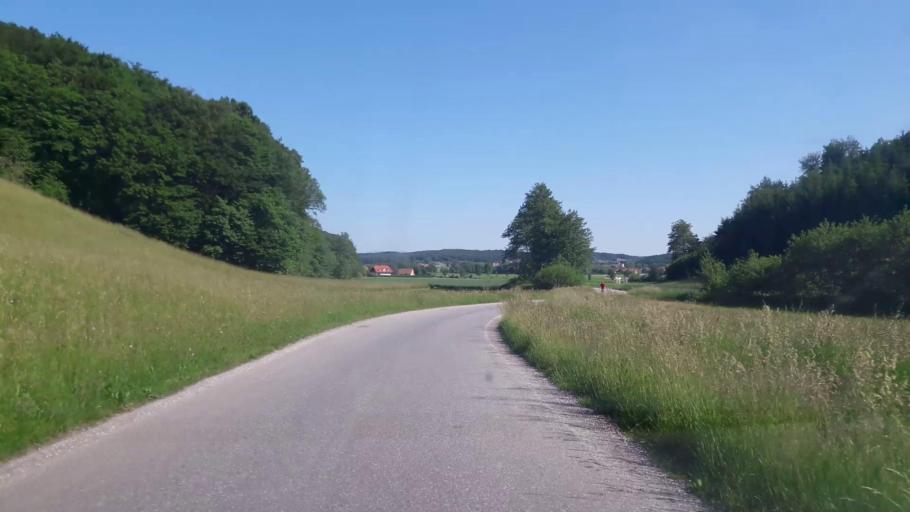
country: AT
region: Styria
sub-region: Politischer Bezirk Hartberg-Fuerstenfeld
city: UEbersbach
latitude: 47.0073
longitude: 16.0509
